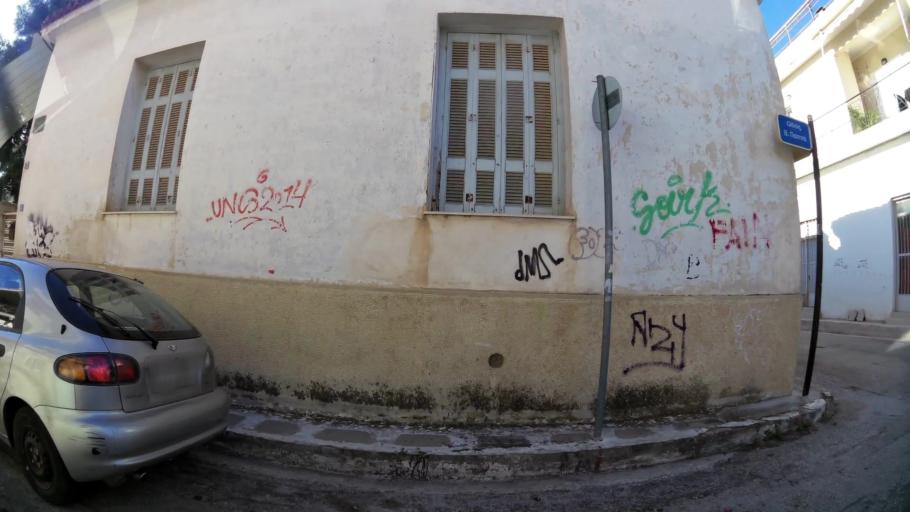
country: GR
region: Attica
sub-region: Nomarchia Anatolikis Attikis
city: Koropi
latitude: 37.9001
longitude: 23.8708
